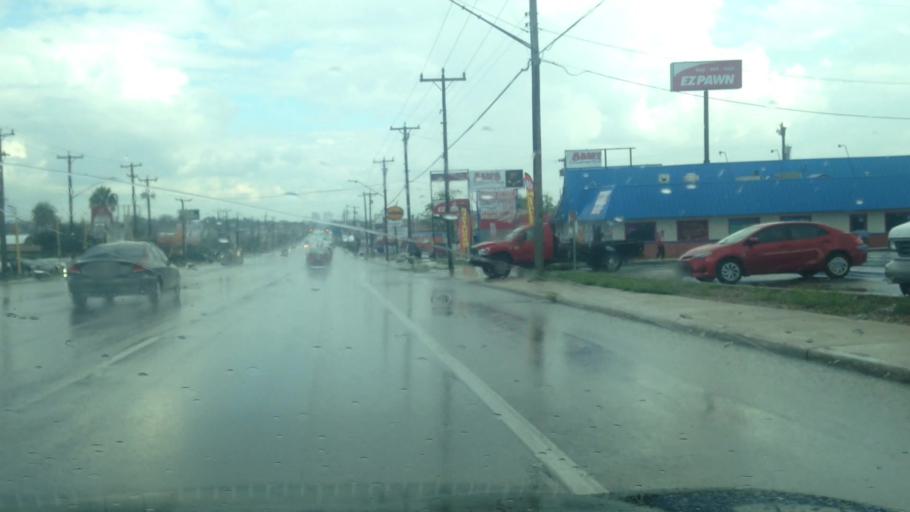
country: US
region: Texas
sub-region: Bexar County
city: Balcones Heights
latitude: 29.4829
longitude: -98.5443
